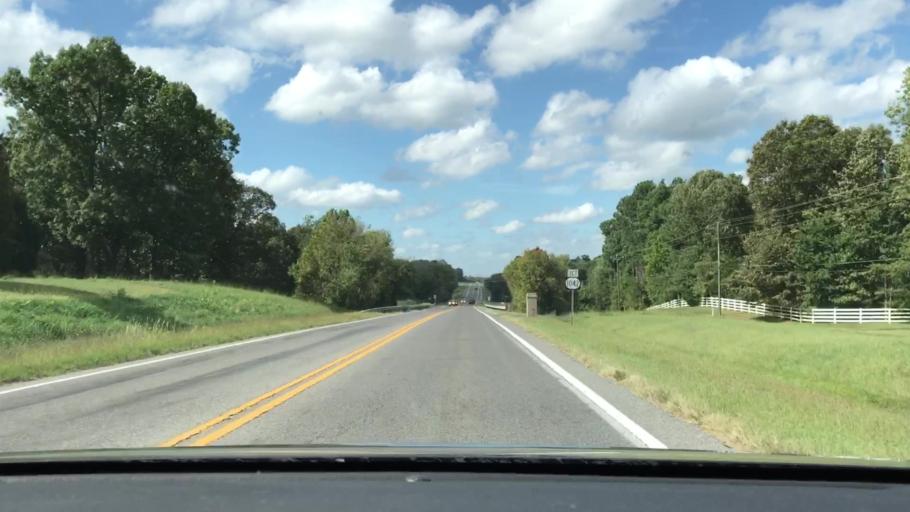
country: US
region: Kentucky
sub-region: Livingston County
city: Ledbetter
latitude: 37.0070
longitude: -88.4658
